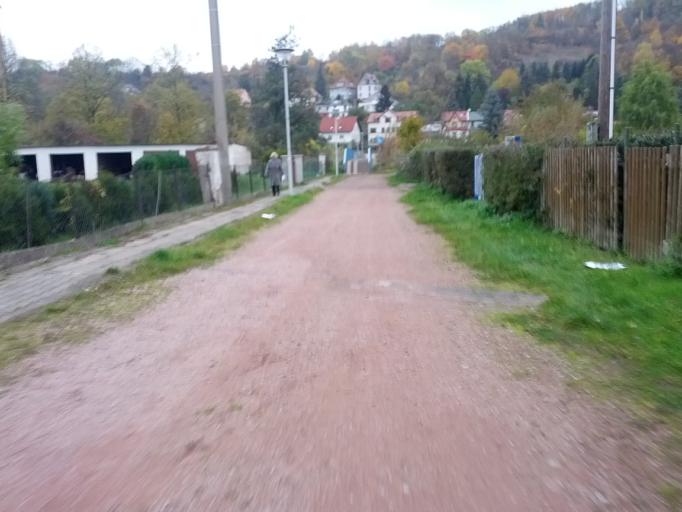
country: DE
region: Thuringia
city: Eisenach
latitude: 50.9796
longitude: 10.3418
